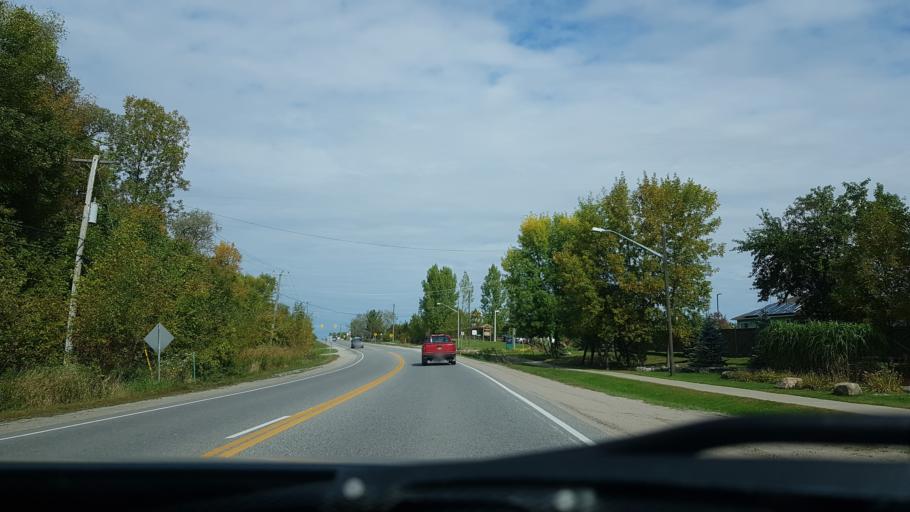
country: CA
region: Ontario
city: Orillia
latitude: 44.6513
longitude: -79.3493
